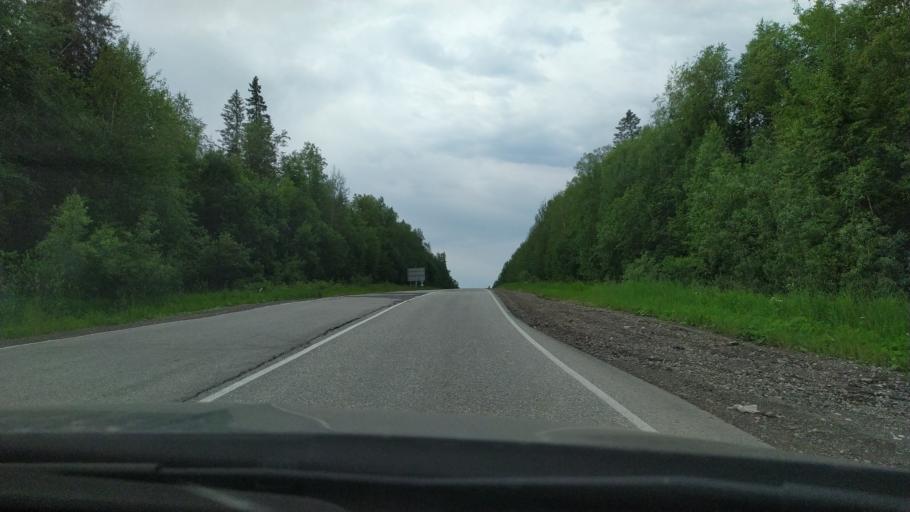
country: RU
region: Perm
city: Gremyachinsk
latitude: 58.4313
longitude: 57.8846
